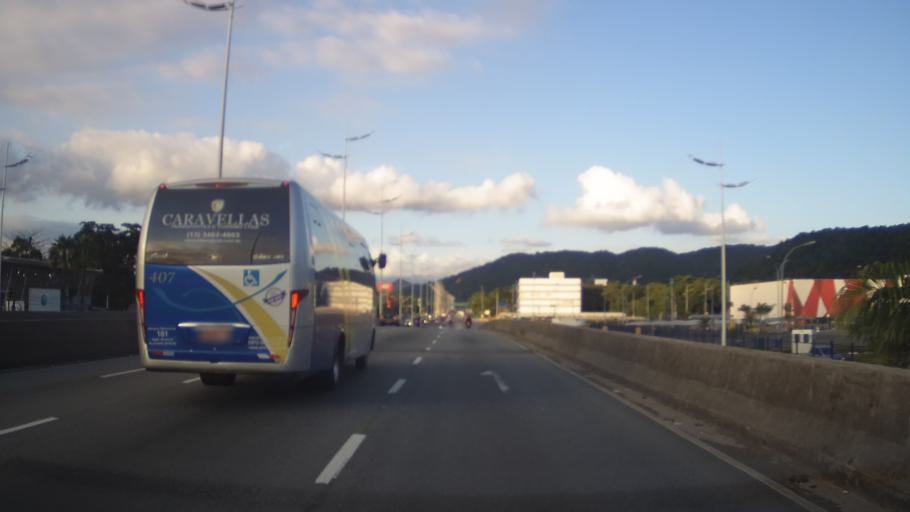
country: BR
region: Sao Paulo
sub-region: Praia Grande
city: Praia Grande
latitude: -23.9966
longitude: -46.4092
